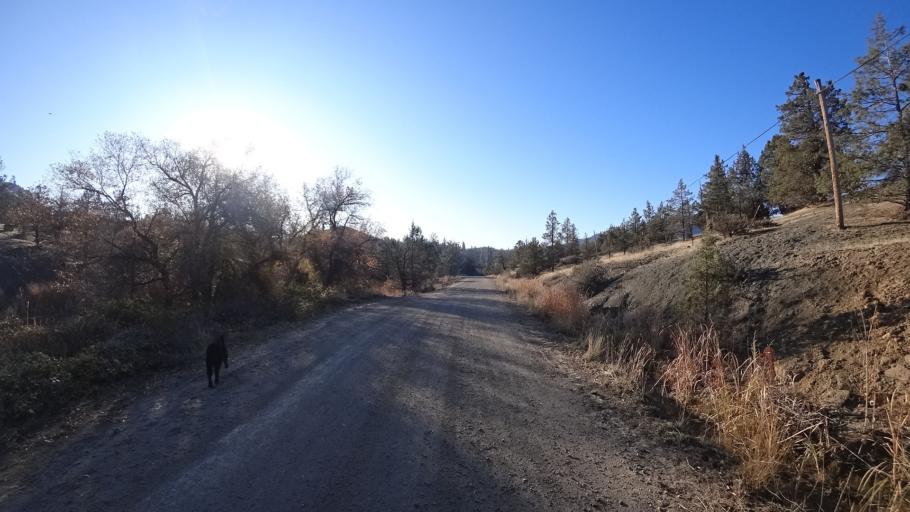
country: US
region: Oregon
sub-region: Jackson County
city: Ashland
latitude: 41.9895
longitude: -122.6228
